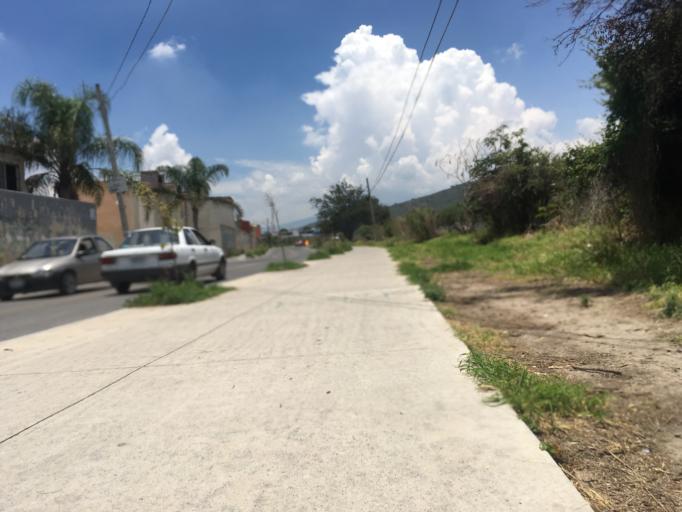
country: MX
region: Jalisco
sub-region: Tlajomulco de Zuniga
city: Jardines de San Sebastian
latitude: 20.5224
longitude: -103.4250
